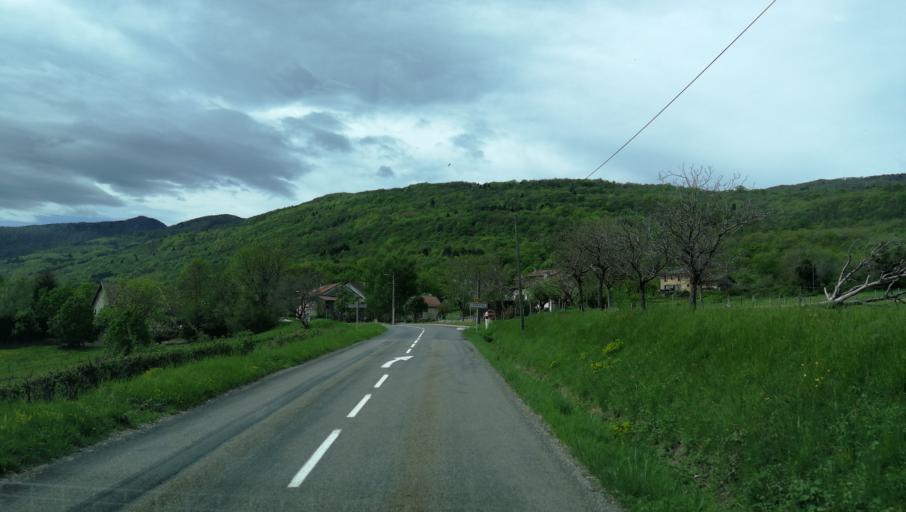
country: FR
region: Rhone-Alpes
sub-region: Departement de l'Ain
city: Bellegarde-sur-Valserine
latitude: 46.0238
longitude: 5.7803
